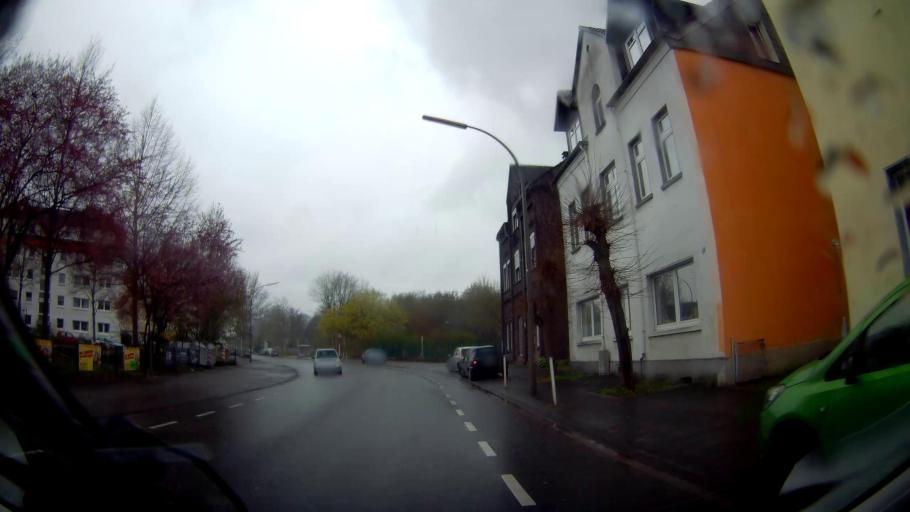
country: DE
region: North Rhine-Westphalia
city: Witten
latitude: 51.5080
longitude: 7.3736
